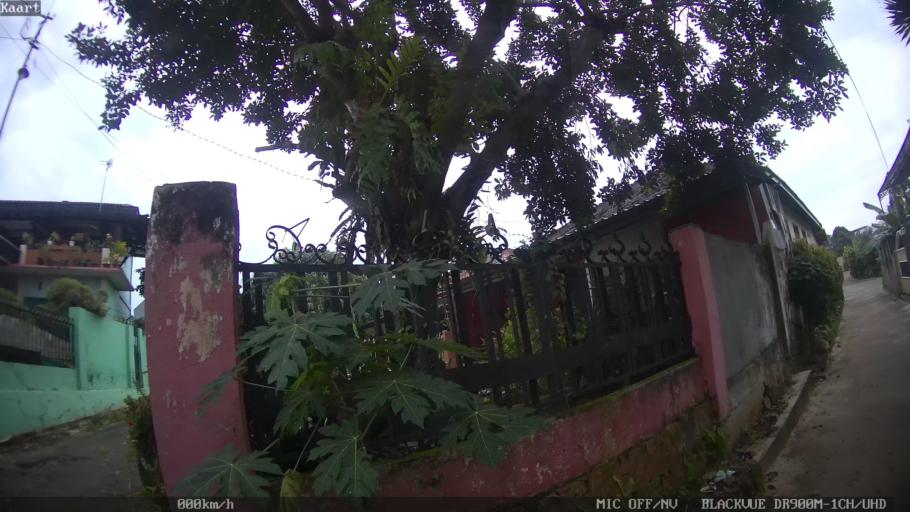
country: ID
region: Lampung
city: Kedaton
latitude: -5.3842
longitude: 105.2516
